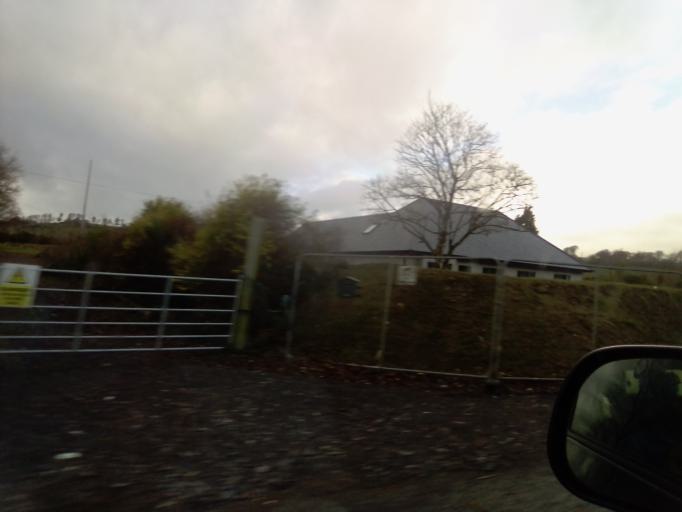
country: IE
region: Leinster
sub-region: Lu
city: Tullyallen
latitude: 53.7894
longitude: -6.4898
